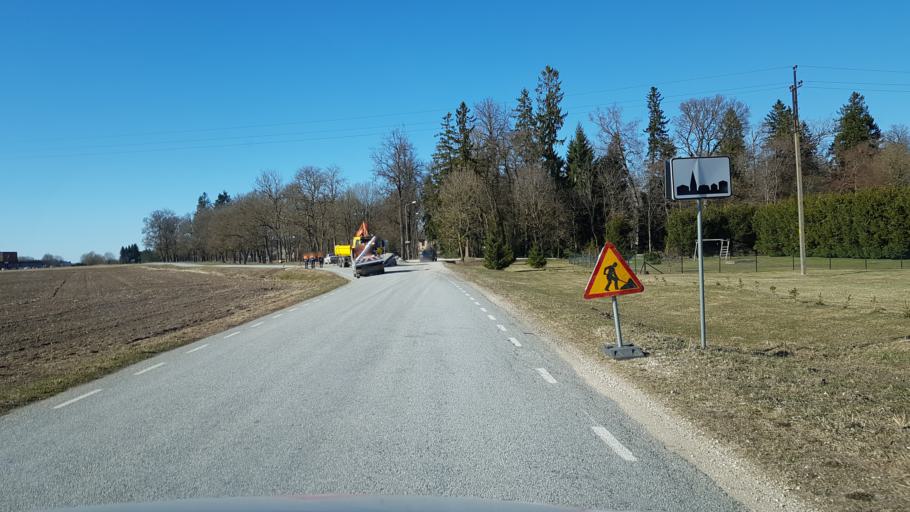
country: EE
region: Laeaene-Virumaa
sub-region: Viru-Nigula vald
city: Kunda
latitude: 59.3911
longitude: 26.5694
